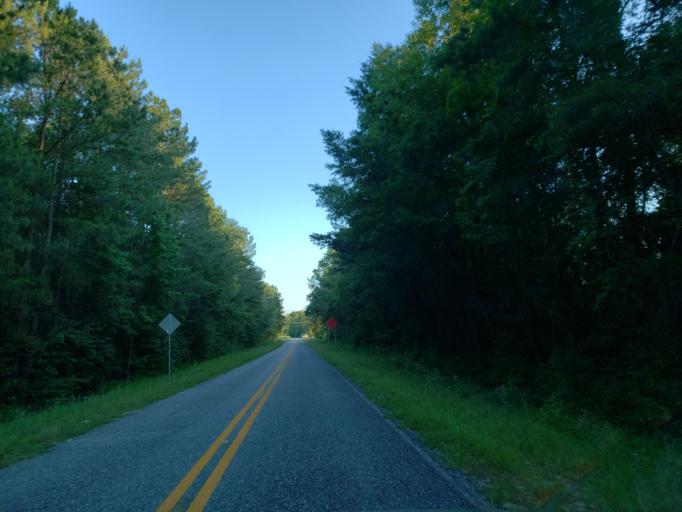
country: US
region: Georgia
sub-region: Crisp County
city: Cordele
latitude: 32.0080
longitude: -83.7546
